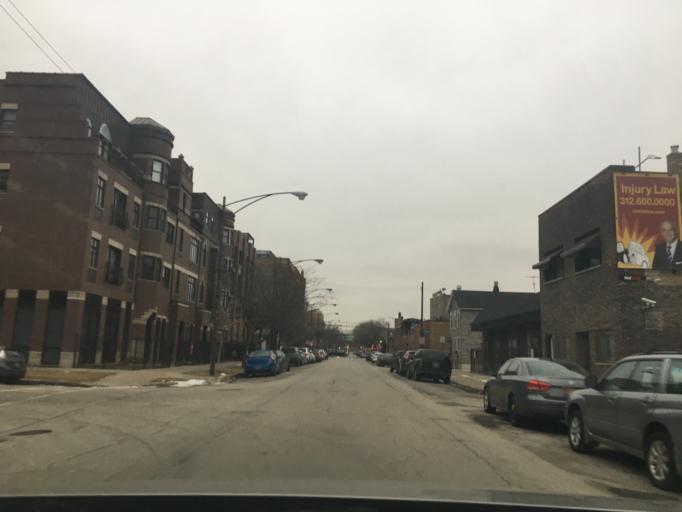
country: US
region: Illinois
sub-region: Cook County
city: Chicago
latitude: 41.8921
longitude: -87.6574
